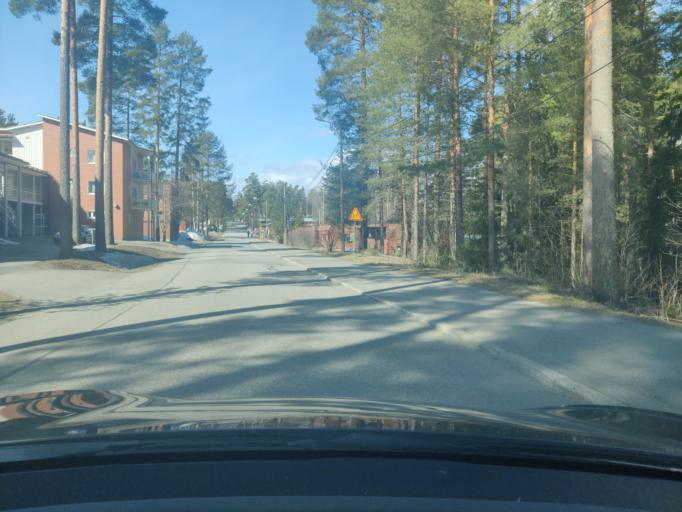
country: FI
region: Northern Savo
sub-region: Kuopio
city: Vehmersalmi
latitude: 62.9142
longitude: 28.1532
